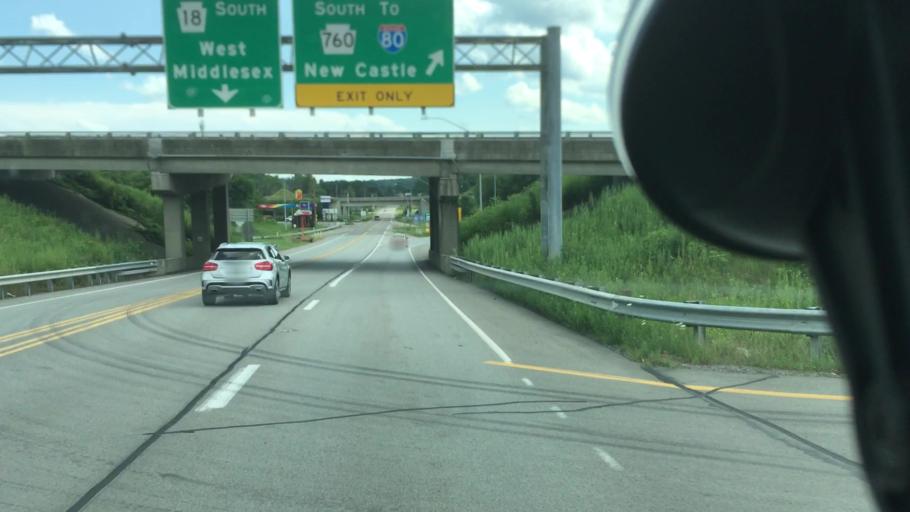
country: US
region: Pennsylvania
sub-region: Mercer County
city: Hermitage
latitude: 41.1877
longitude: -80.4560
